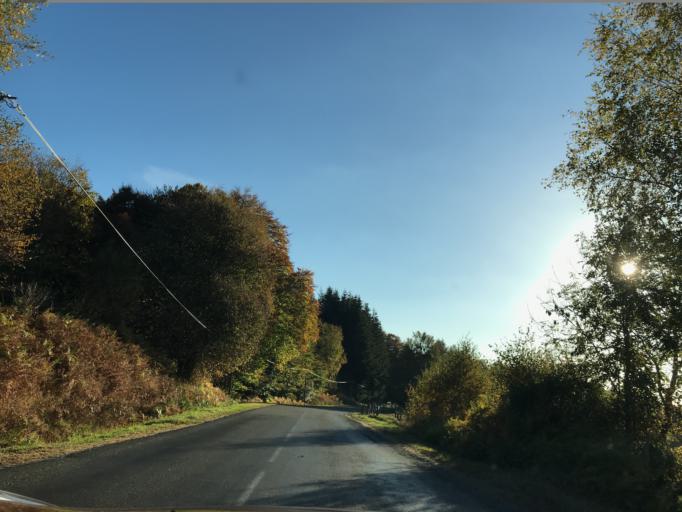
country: FR
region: Rhone-Alpes
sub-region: Departement de la Loire
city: Noiretable
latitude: 45.7922
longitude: 3.6926
